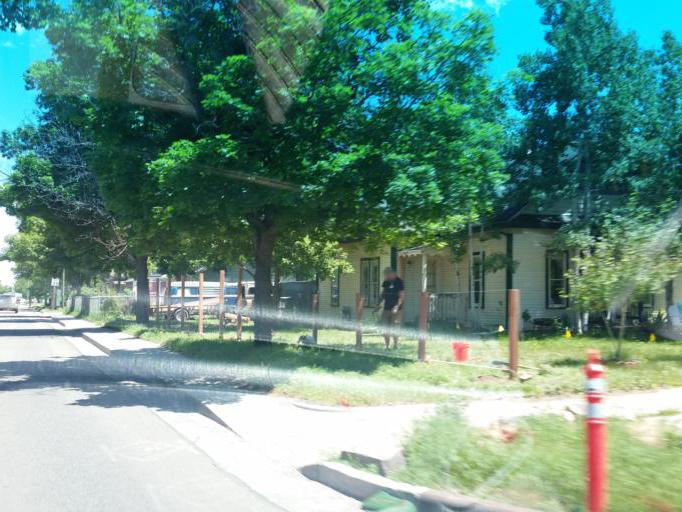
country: US
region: Colorado
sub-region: Larimer County
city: Fort Collins
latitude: 40.5814
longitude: -105.0684
